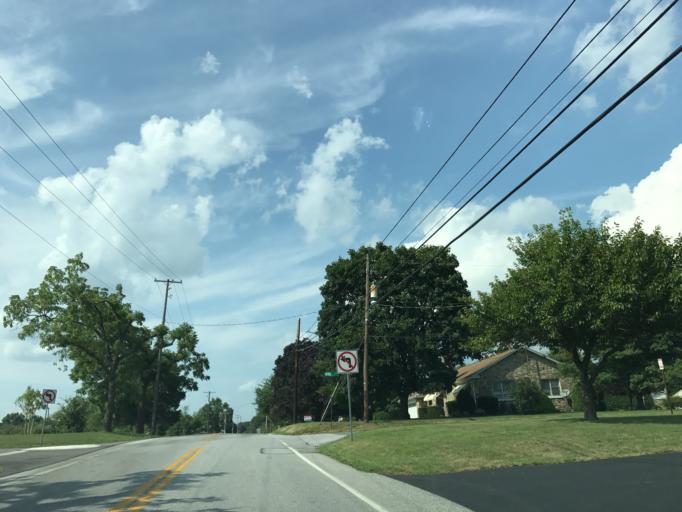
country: US
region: Pennsylvania
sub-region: York County
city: Pennville
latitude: 39.7677
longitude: -76.9929
